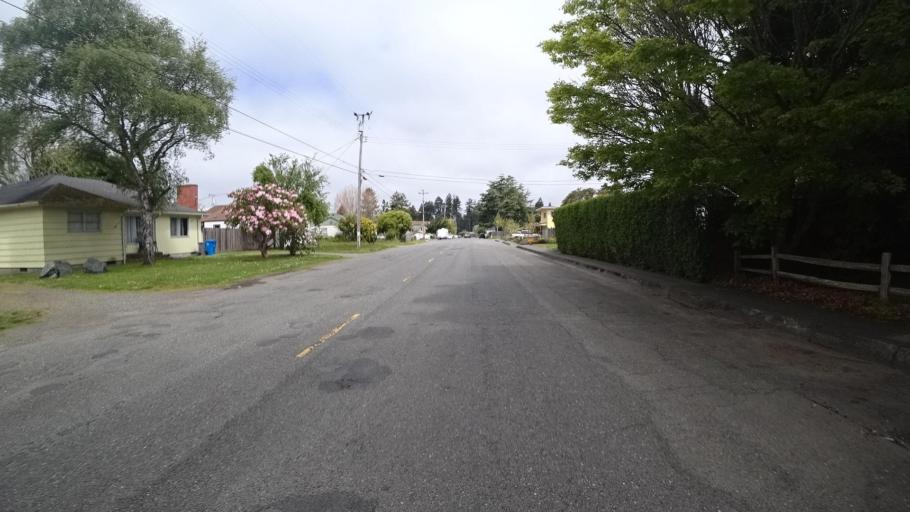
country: US
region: California
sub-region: Humboldt County
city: Cutten
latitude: 40.7691
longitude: -124.1413
